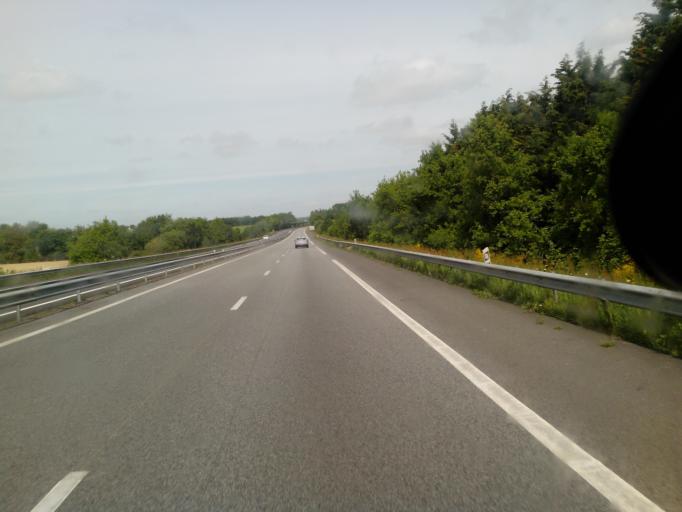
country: FR
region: Pays de la Loire
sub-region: Departement de la Loire-Atlantique
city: Derval
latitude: 47.6821
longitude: -1.6959
